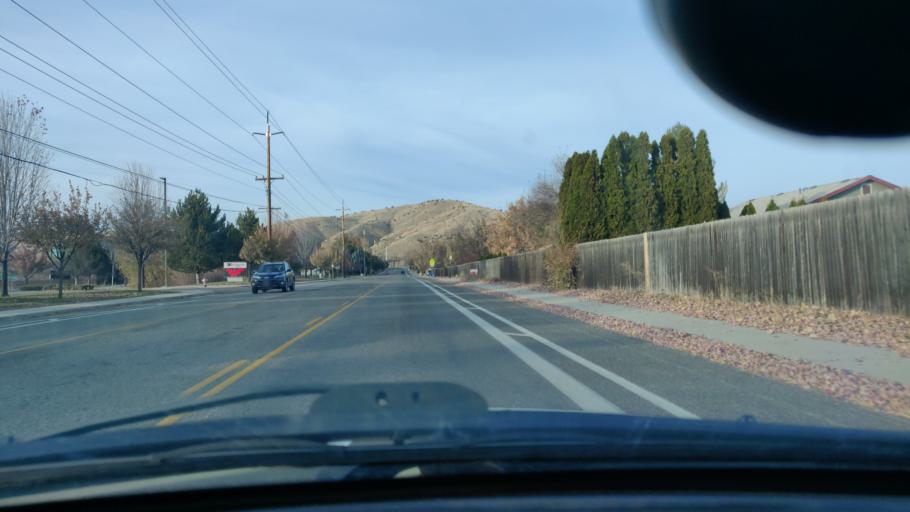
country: US
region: Idaho
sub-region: Ada County
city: Garden City
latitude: 43.6787
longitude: -116.2792
